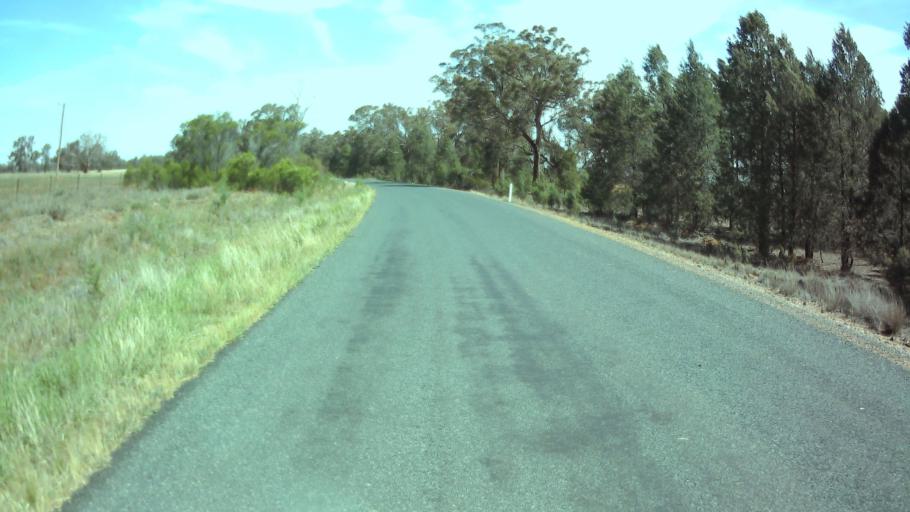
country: AU
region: New South Wales
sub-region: Weddin
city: Grenfell
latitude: -34.0547
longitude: 148.1299
